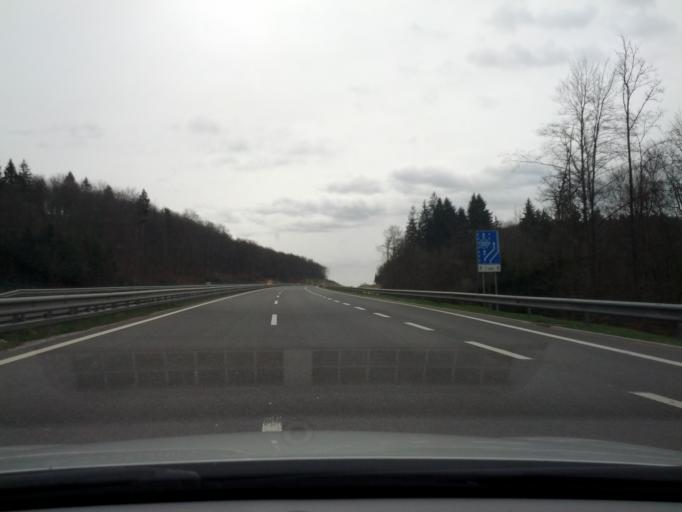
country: SI
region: Mirna Pec
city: Mirna Pec
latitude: 45.8859
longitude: 15.0709
